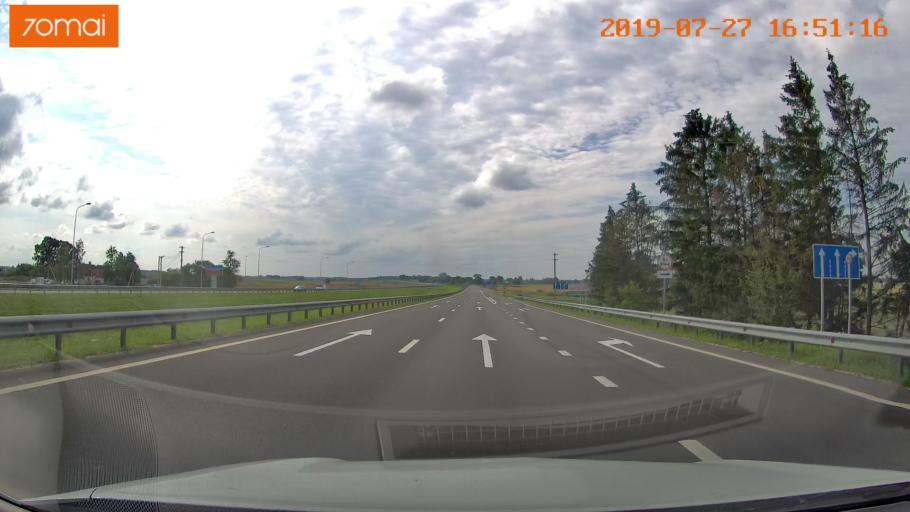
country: RU
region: Kaliningrad
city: Gvardeysk
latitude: 54.6819
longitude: 20.8911
